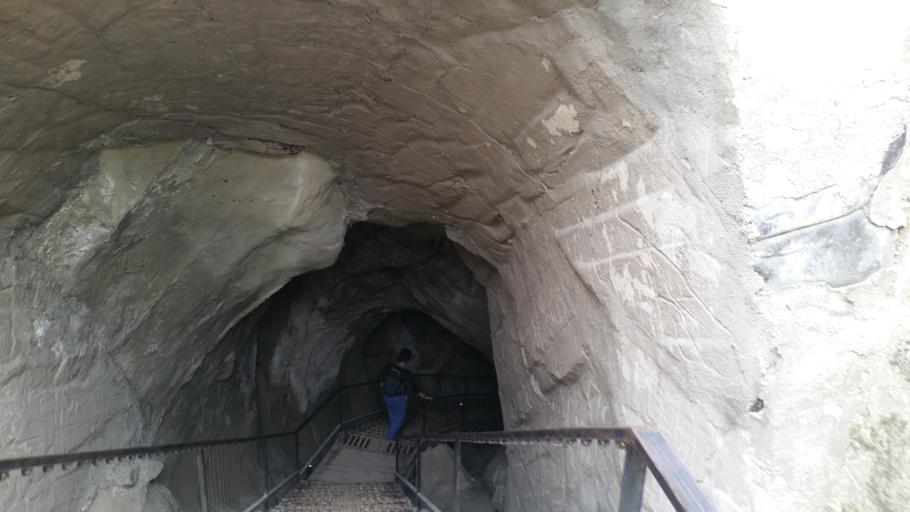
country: GE
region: Shida Kartli
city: Gori
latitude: 41.9662
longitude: 44.2073
